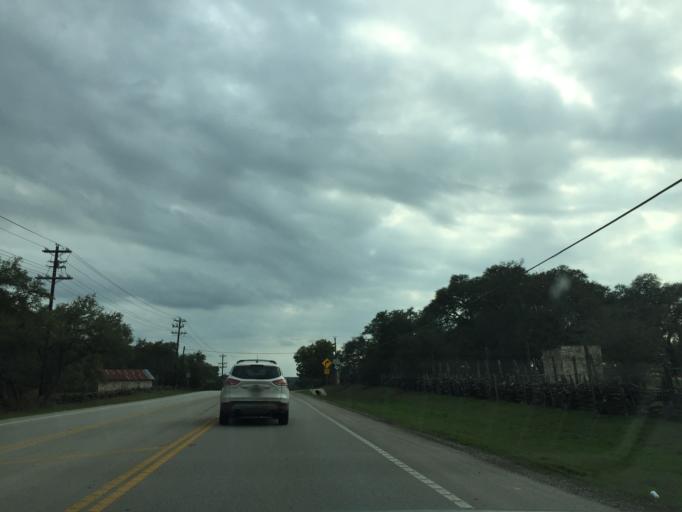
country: US
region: Texas
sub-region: Hays County
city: Dripping Springs
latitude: 30.1343
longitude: -98.0087
